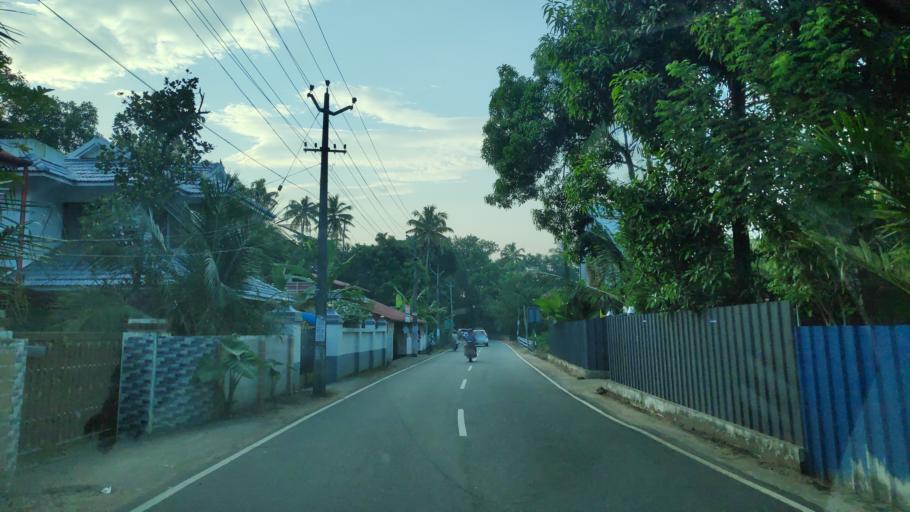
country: IN
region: Kerala
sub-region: Alappuzha
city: Shertallai
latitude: 9.6783
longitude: 76.3898
